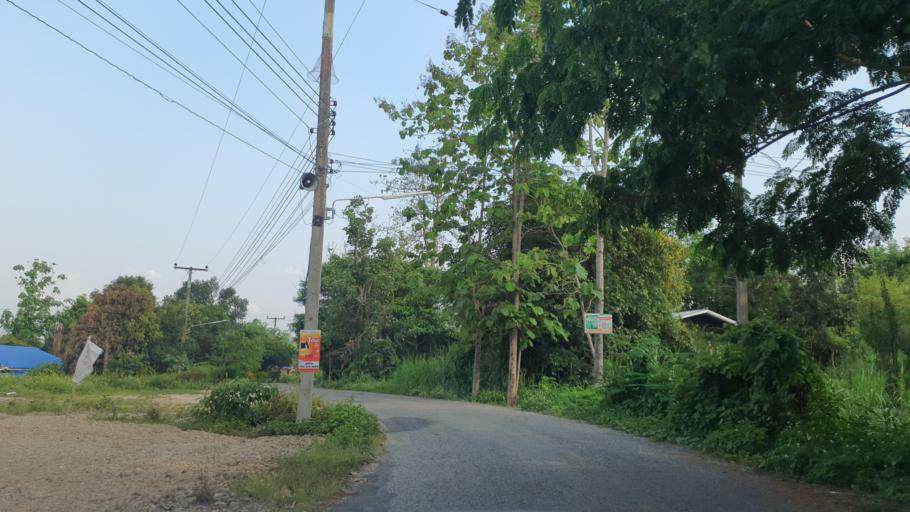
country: TH
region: Chiang Mai
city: Mae Wang
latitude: 18.6801
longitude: 98.8093
